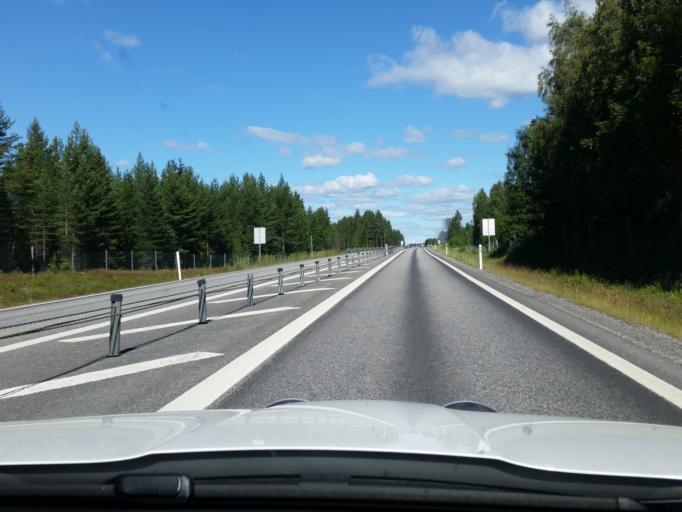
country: SE
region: Norrbotten
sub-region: Pitea Kommun
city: Pitea
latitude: 65.2671
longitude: 21.4595
